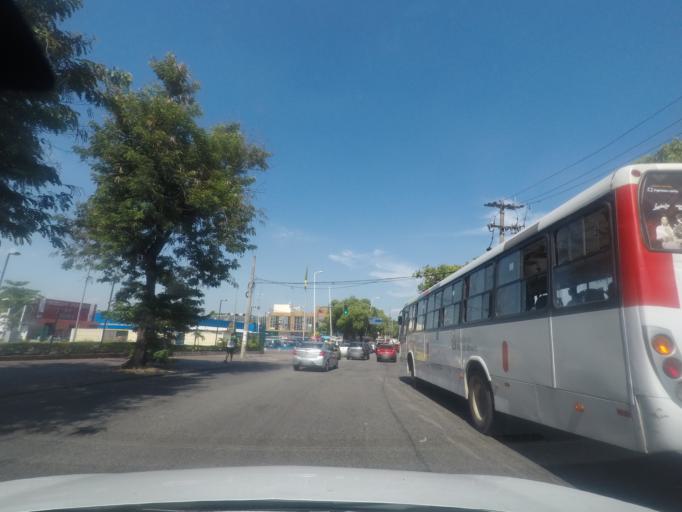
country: BR
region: Rio de Janeiro
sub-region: Nilopolis
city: Nilopolis
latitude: -22.8798
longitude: -43.4661
